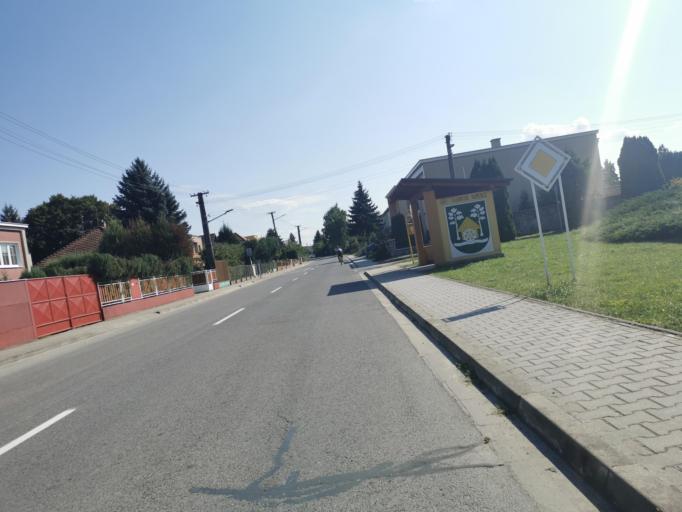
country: SK
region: Trnavsky
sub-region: Okres Senica
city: Senica
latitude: 48.6598
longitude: 17.2640
